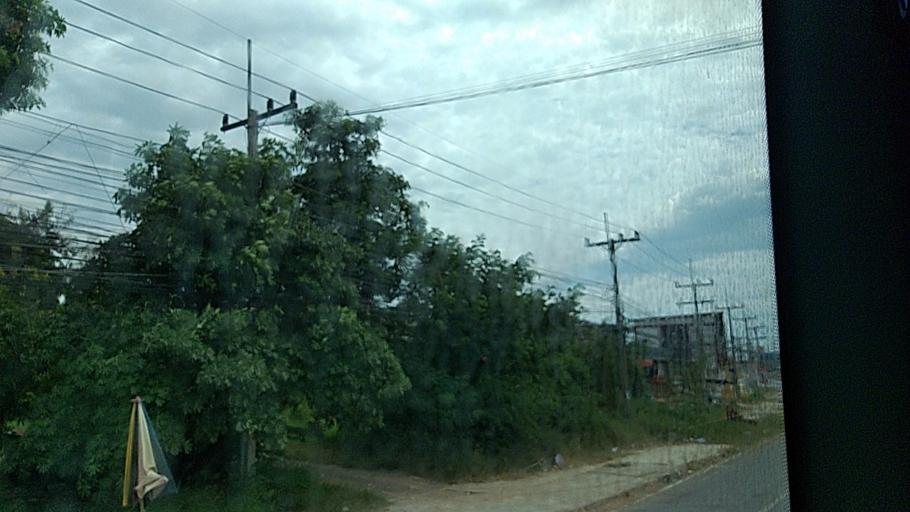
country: TH
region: Maha Sarakham
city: Maha Sarakham
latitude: 16.2254
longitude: 103.2715
